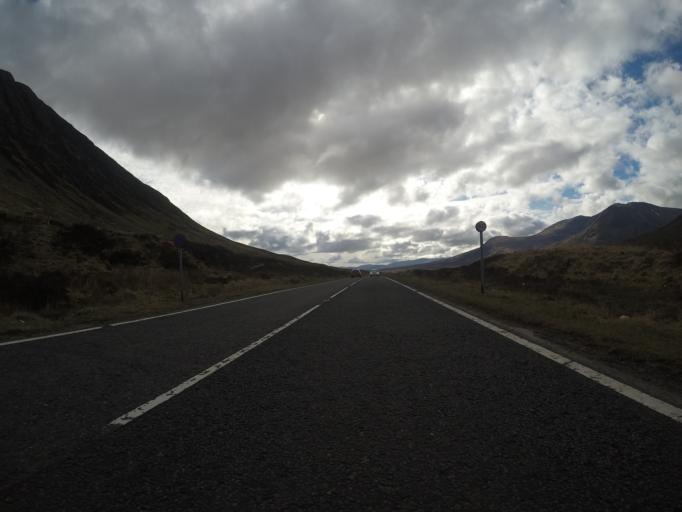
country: GB
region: Scotland
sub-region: Highland
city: Spean Bridge
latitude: 56.6615
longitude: -4.8919
